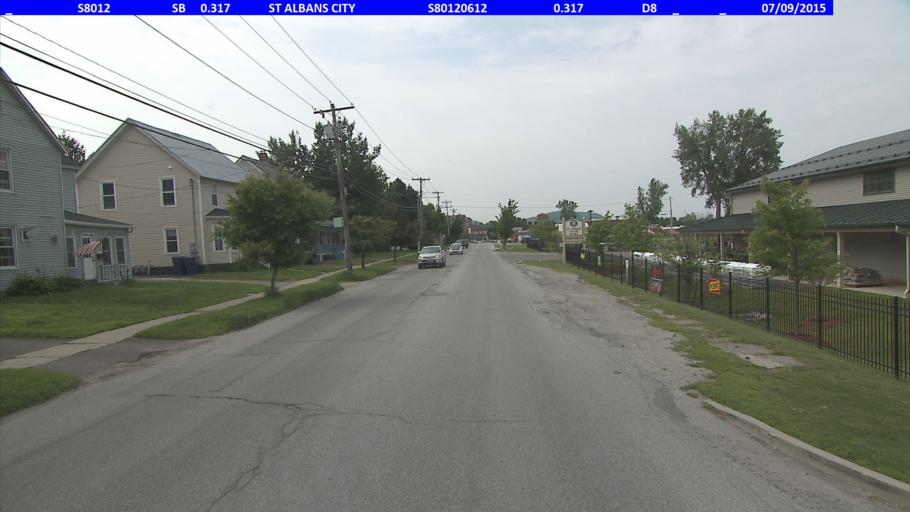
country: US
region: Vermont
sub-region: Franklin County
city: Saint Albans
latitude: 44.8154
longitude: -73.0849
